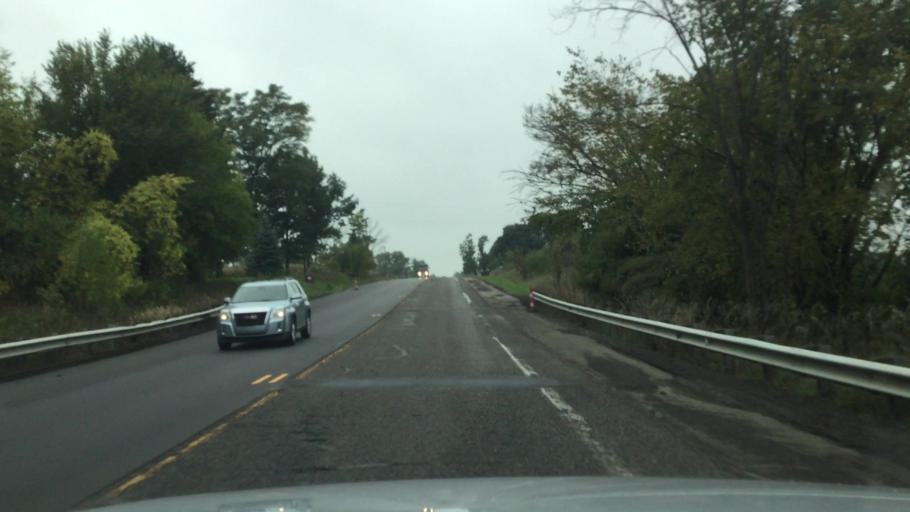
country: US
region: Michigan
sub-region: Shiawassee County
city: Perry
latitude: 42.9124
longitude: -84.2223
